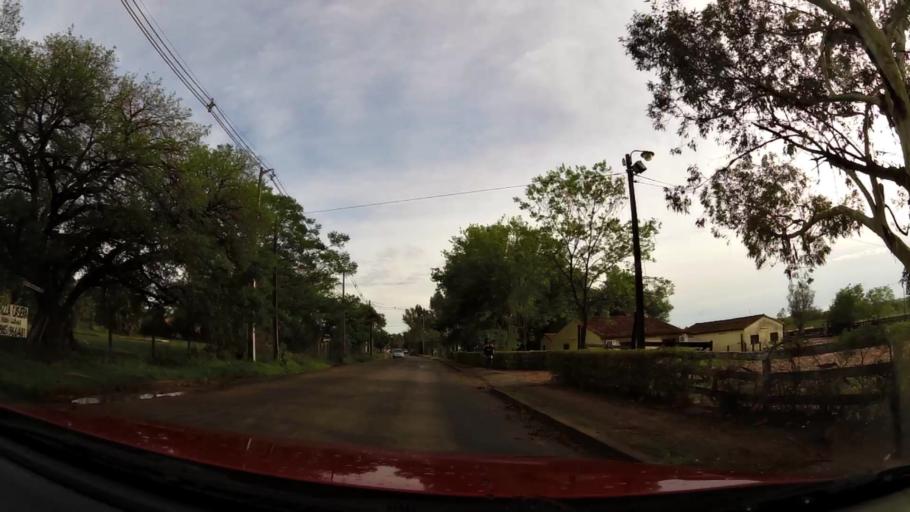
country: PY
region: Central
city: Limpio
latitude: -25.1952
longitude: -57.5032
